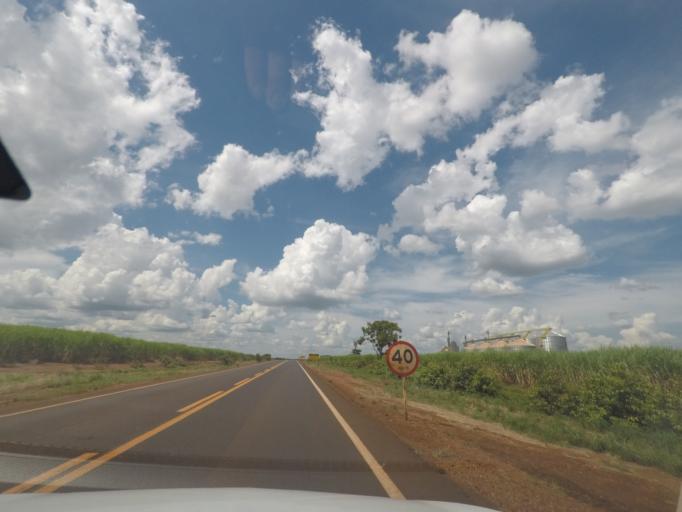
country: BR
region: Minas Gerais
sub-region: Conceicao Das Alagoas
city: Conceicao das Alagoas
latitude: -19.8090
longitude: -48.5825
